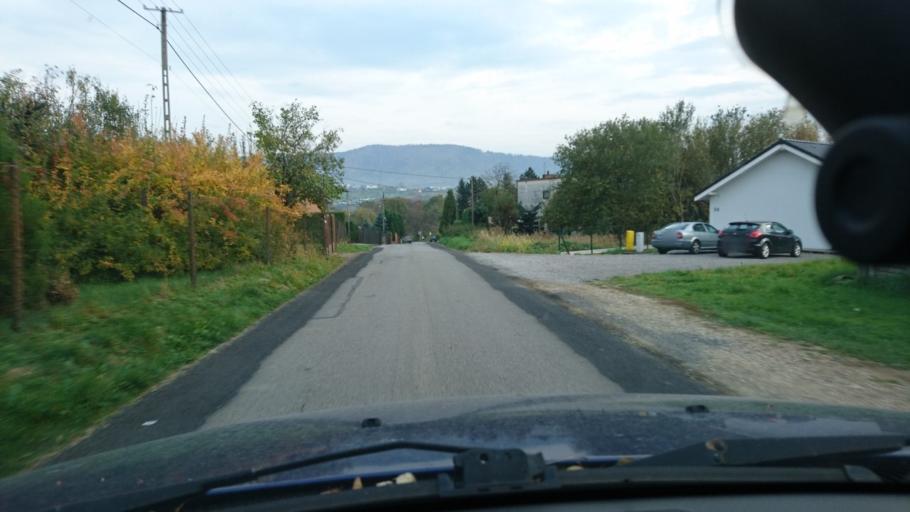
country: PL
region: Silesian Voivodeship
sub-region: Bielsko-Biala
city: Bielsko-Biala
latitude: 49.8359
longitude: 19.0789
